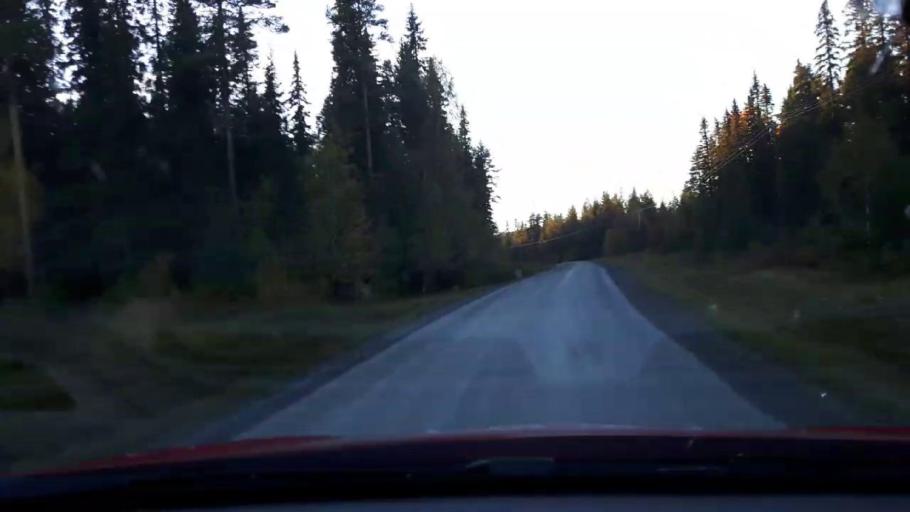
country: SE
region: Jaemtland
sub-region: Krokoms Kommun
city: Krokom
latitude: 63.4761
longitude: 14.2580
